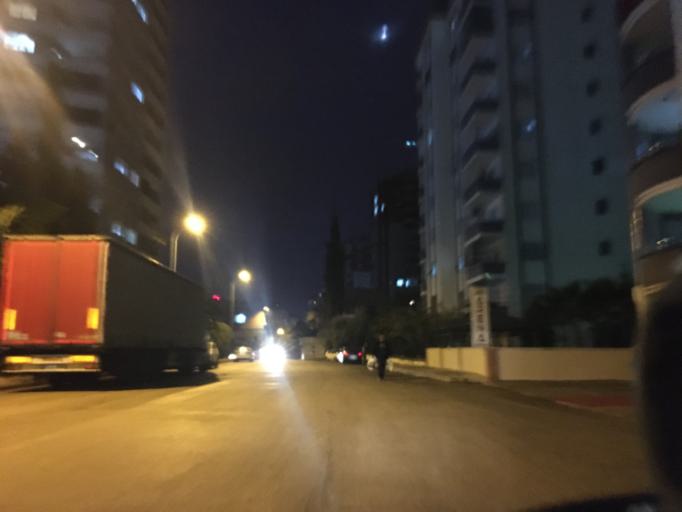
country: TR
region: Adana
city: Seyhan
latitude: 37.0265
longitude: 35.2832
